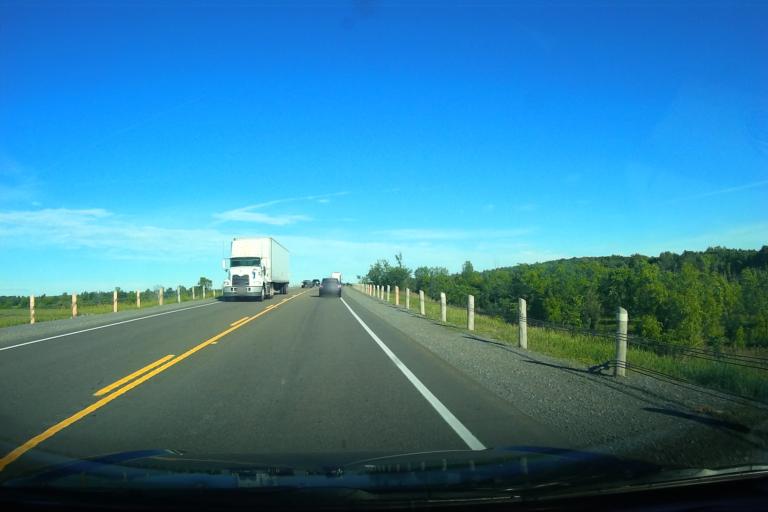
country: CA
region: Ontario
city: Renfrew
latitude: 45.4779
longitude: -76.6344
